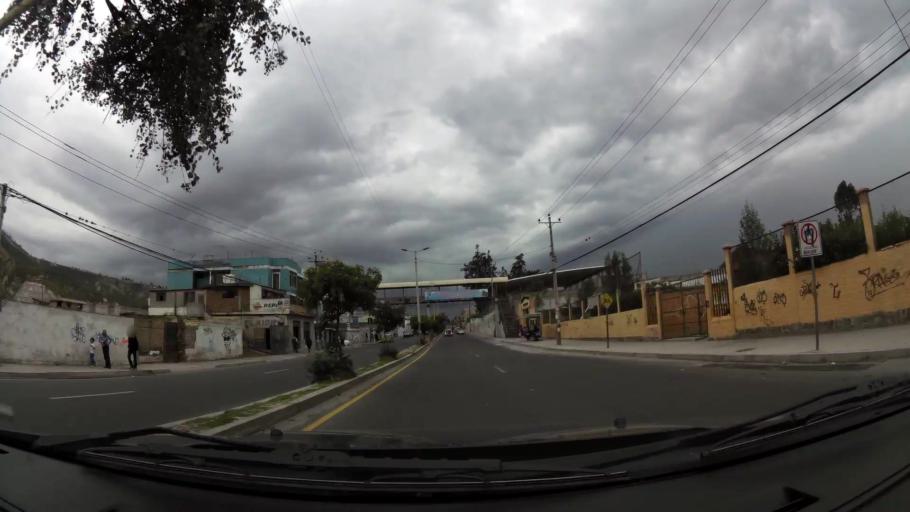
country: EC
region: Pichincha
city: Quito
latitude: -0.0521
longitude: -78.4563
